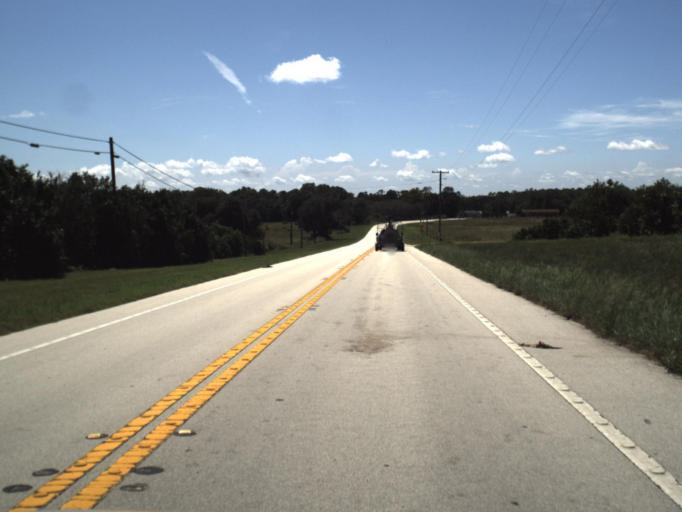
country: US
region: Florida
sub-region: Polk County
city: Frostproof
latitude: 27.7055
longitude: -81.5309
